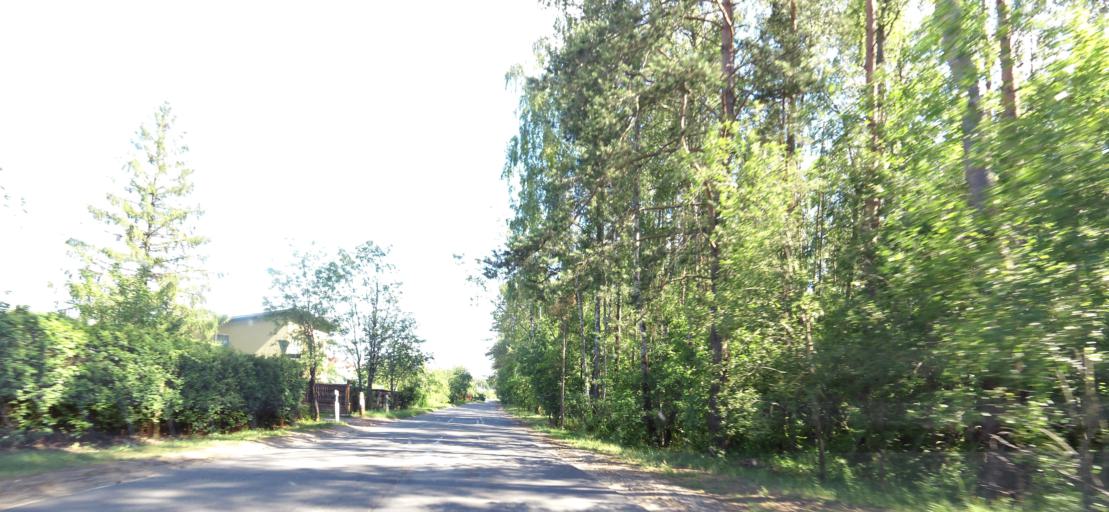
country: LT
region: Vilnius County
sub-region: Vilnius
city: Fabijoniskes
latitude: 54.8023
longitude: 25.3305
